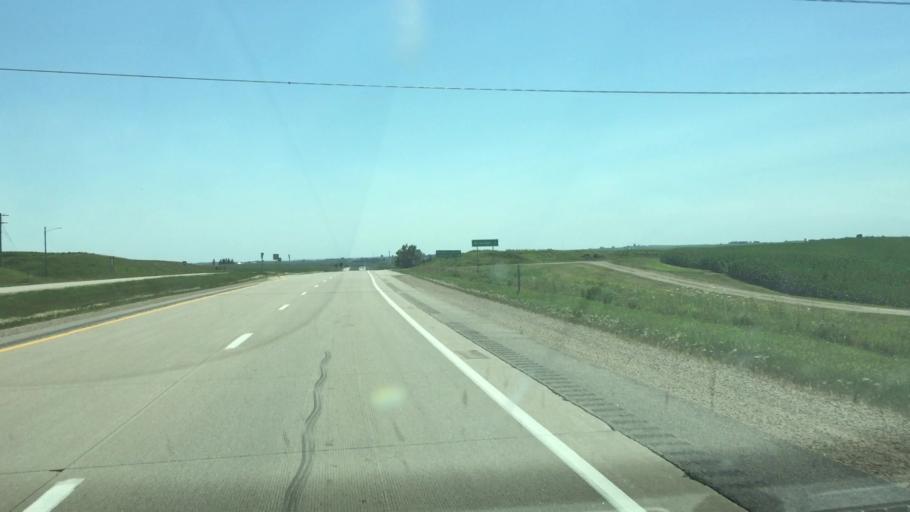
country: US
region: Iowa
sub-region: Dubuque County
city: Peosta
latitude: 42.3642
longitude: -90.8011
